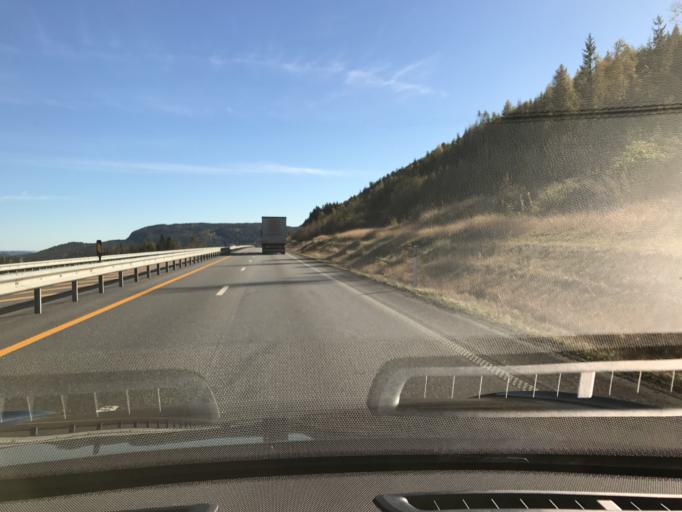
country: NO
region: Buskerud
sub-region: Krodsherad
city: Noresund
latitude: 60.2846
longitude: 9.7521
